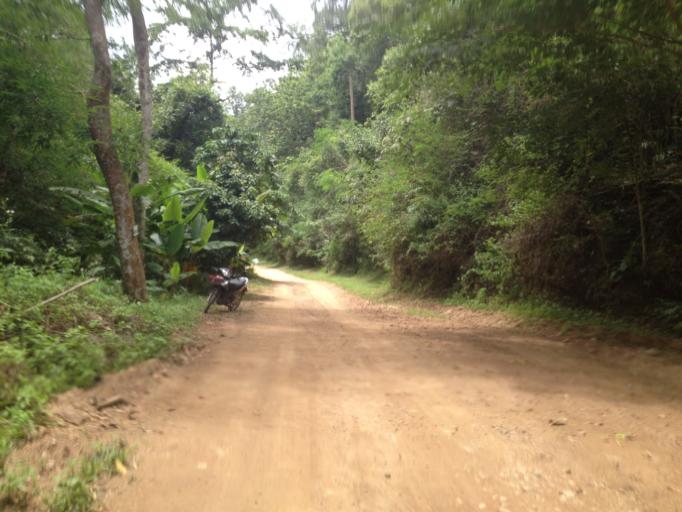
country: TH
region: Chiang Mai
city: Hang Dong
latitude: 18.7189
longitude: 98.8266
